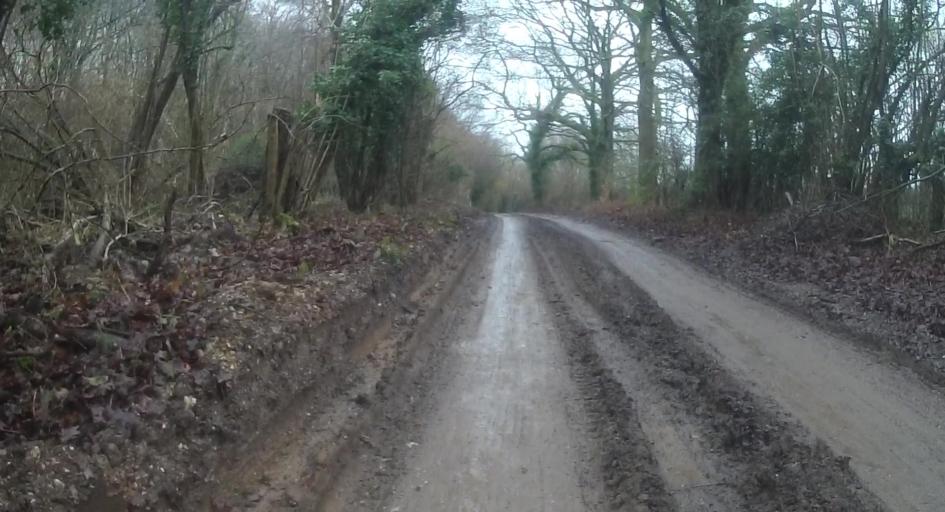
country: GB
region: England
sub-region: Hampshire
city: Kings Worthy
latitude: 51.1149
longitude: -1.2529
